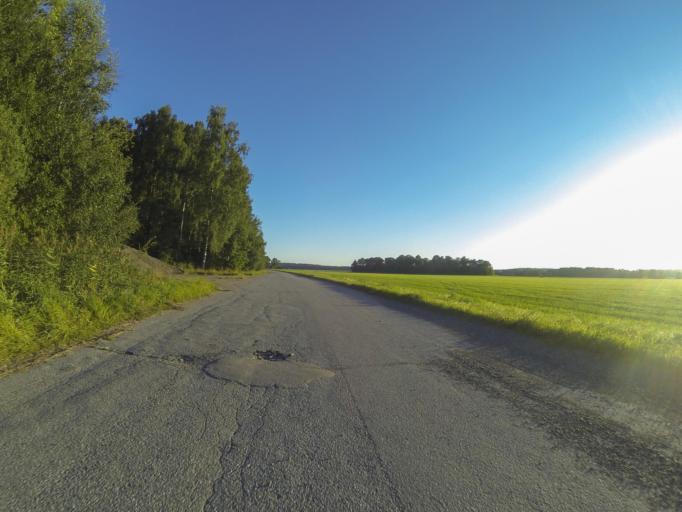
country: SE
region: Vaestmanland
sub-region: Vasteras
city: Vasteras
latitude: 59.5766
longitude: 16.6550
